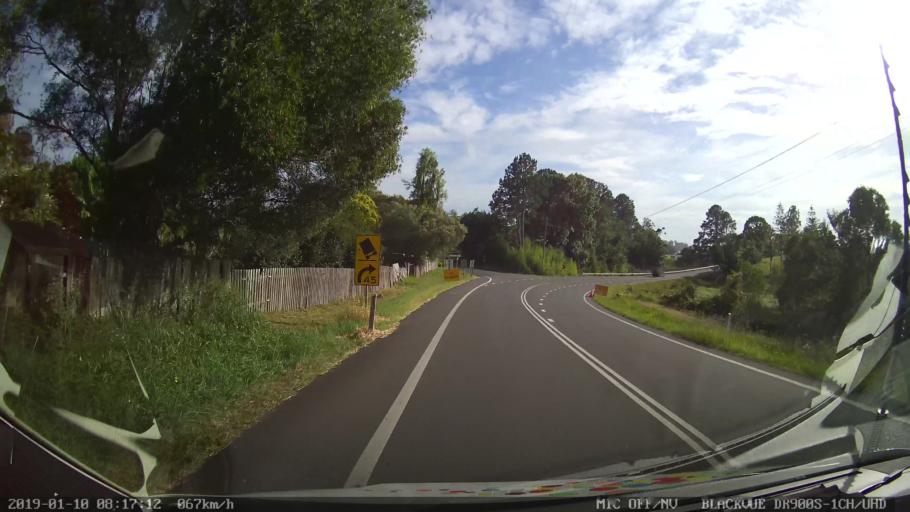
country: AU
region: New South Wales
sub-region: Bellingen
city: Bellingen
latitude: -30.4695
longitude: 152.9400
